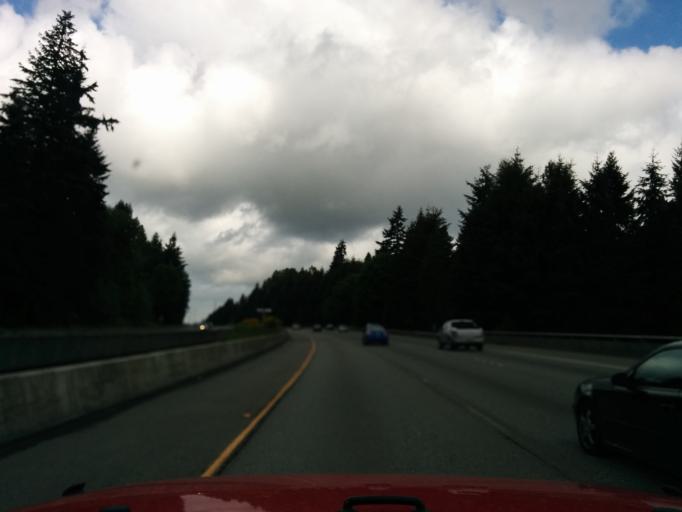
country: US
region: Washington
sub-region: Snohomish County
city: Martha Lake
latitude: 47.8199
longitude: -122.2420
